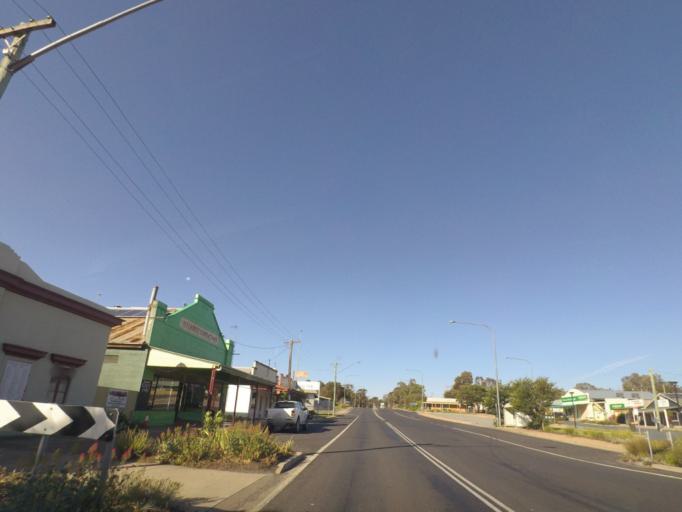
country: AU
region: New South Wales
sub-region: Wagga Wagga
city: Forest Hill
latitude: -35.2768
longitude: 147.7372
